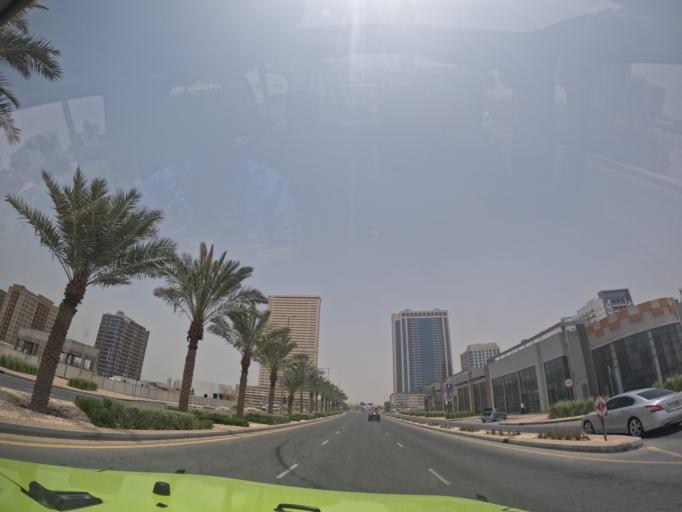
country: AE
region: Dubai
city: Dubai
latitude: 25.0923
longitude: 55.3806
